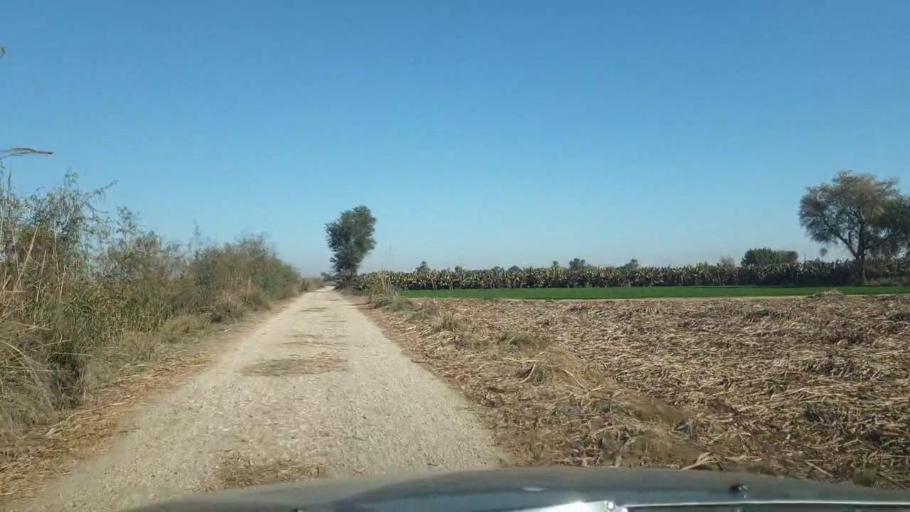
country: PK
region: Sindh
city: Ghotki
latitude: 28.0218
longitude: 69.2839
